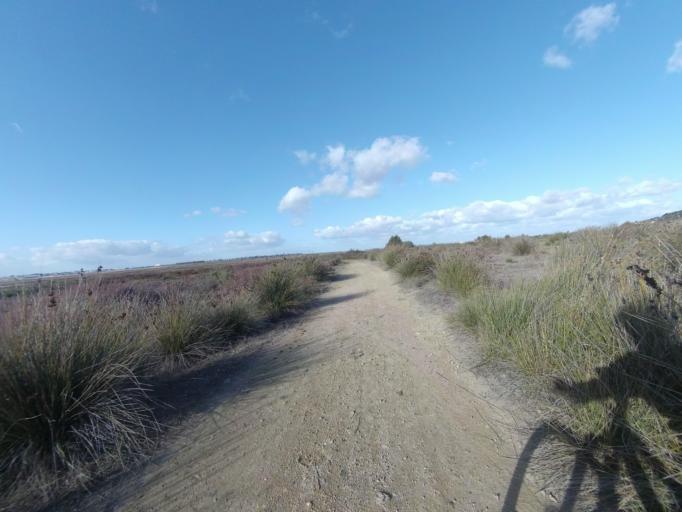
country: ES
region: Andalusia
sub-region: Provincia de Huelva
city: Palos de la Frontera
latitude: 37.2481
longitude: -6.8834
